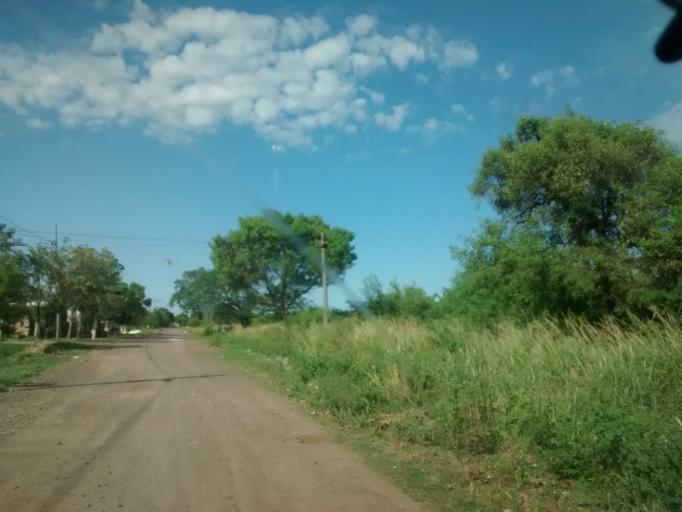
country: AR
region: Chaco
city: Puerto Tirol
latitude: -27.3710
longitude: -59.0986
